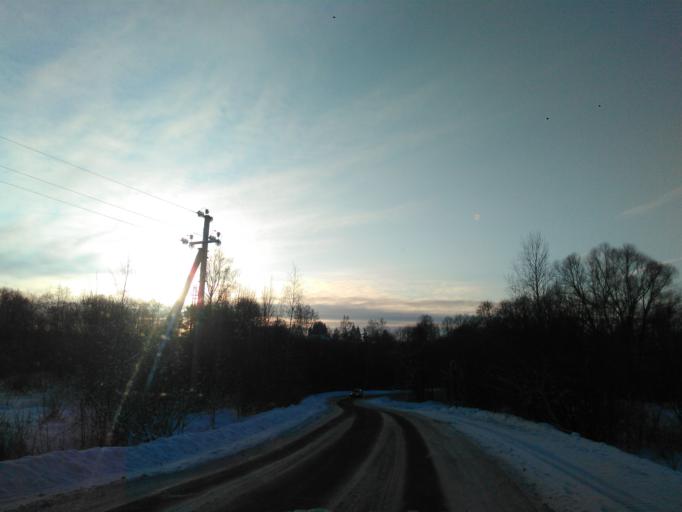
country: RU
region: Tverskaya
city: Zavidovo
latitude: 56.6141
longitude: 36.6185
